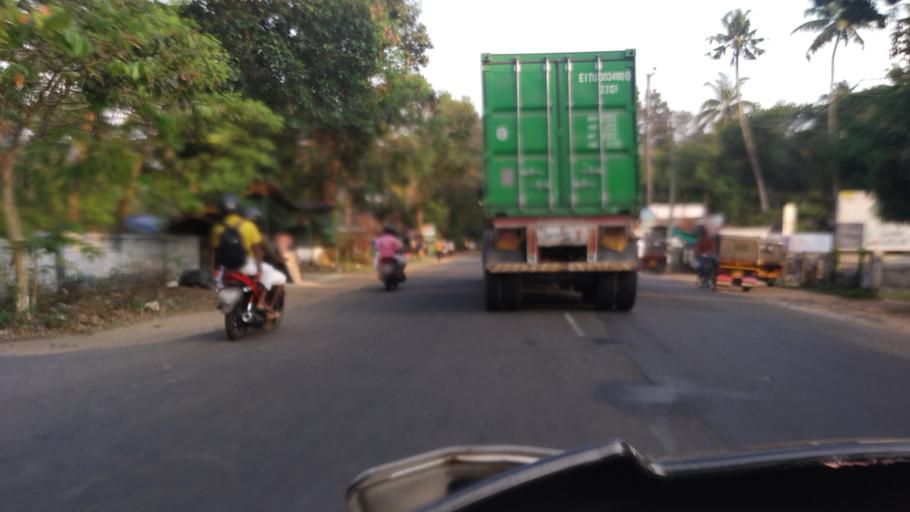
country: IN
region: Kerala
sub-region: Thrissur District
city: Thanniyam
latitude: 10.3446
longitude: 76.1350
